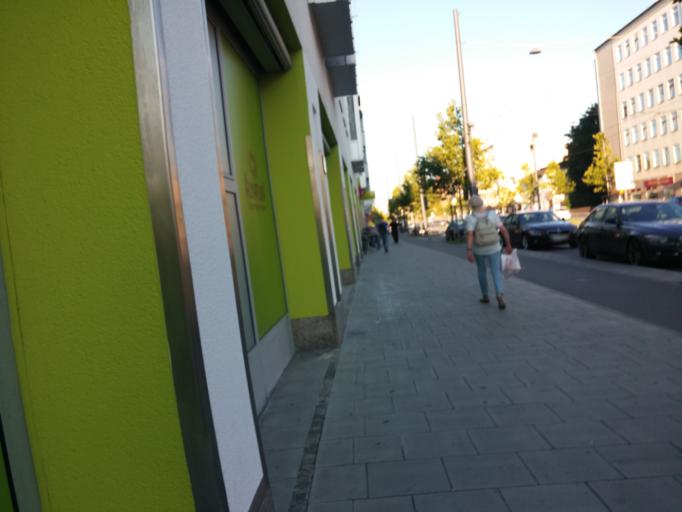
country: DE
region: Bavaria
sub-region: Upper Bavaria
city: Pasing
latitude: 48.1464
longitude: 11.4637
